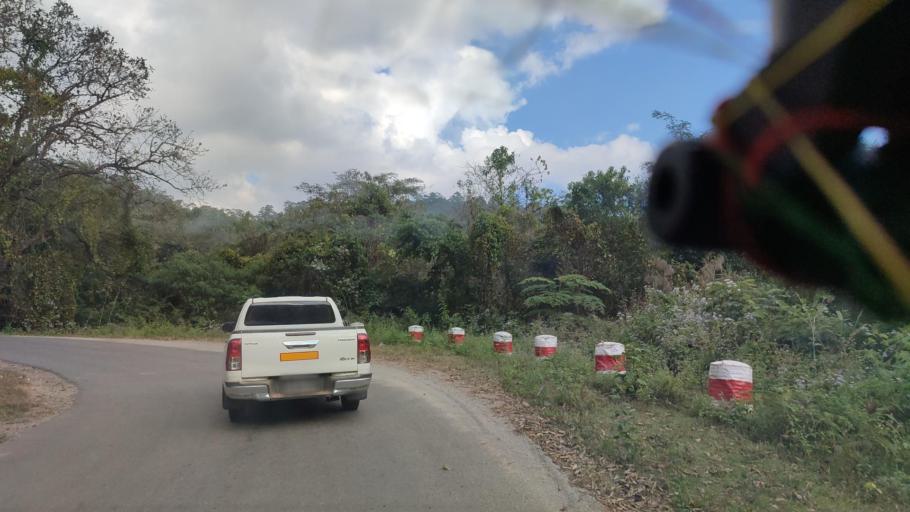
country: MM
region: Shan
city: Taunggyi
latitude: 21.4636
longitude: 97.5945
